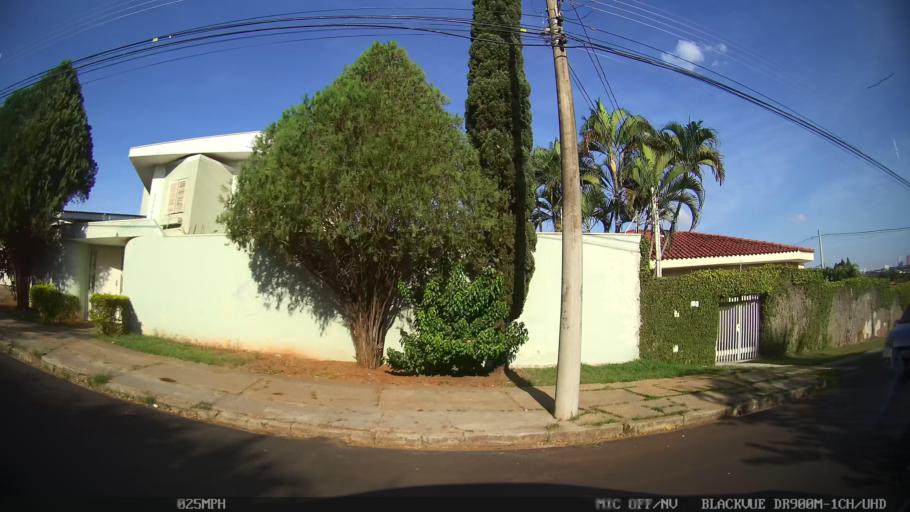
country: BR
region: Sao Paulo
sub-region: Ribeirao Preto
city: Ribeirao Preto
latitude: -21.2046
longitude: -47.7785
